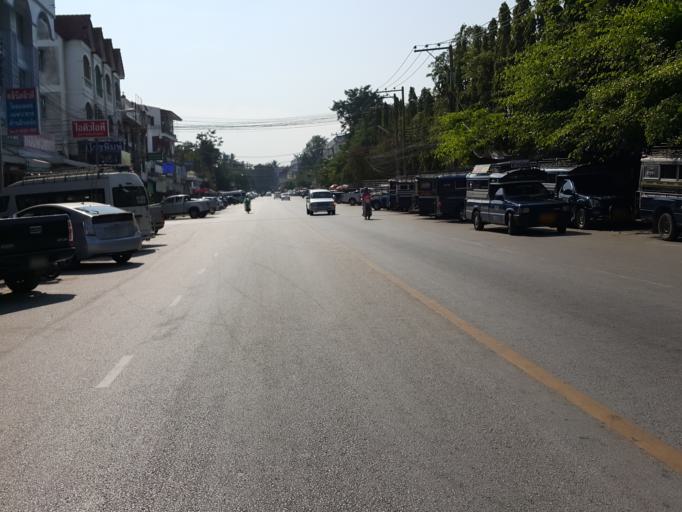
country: TH
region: Lampang
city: Lampang
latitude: 18.2875
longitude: 99.5036
